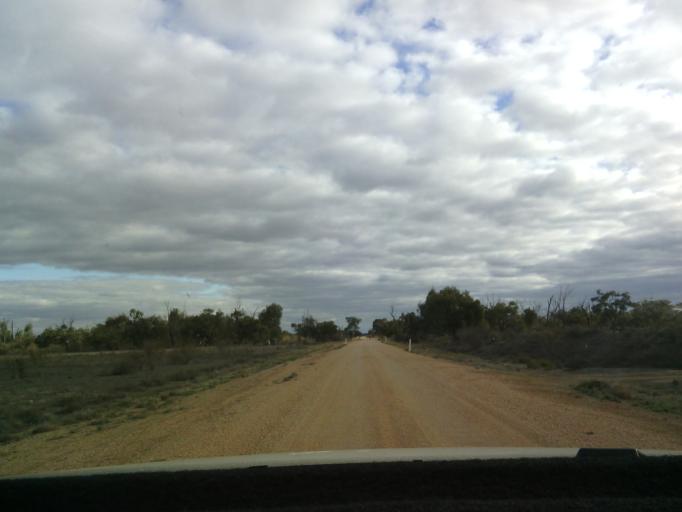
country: AU
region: South Australia
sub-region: Renmark Paringa
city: Renmark
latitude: -34.1652
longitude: 141.1921
